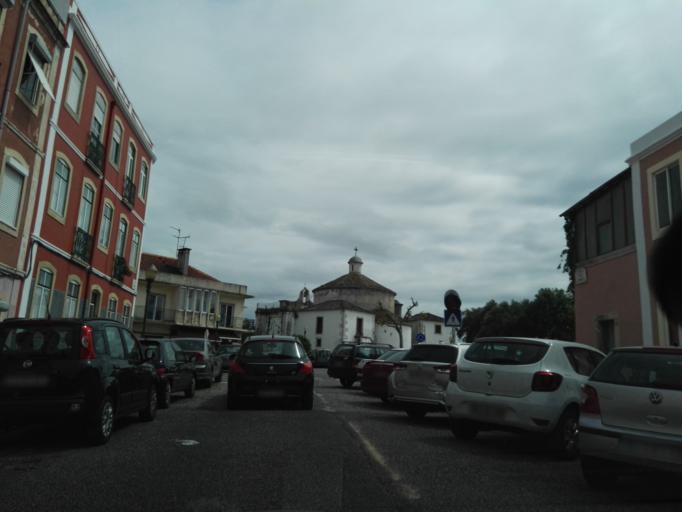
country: PT
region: Setubal
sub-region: Almada
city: Pragal
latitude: 38.7027
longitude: -9.1830
